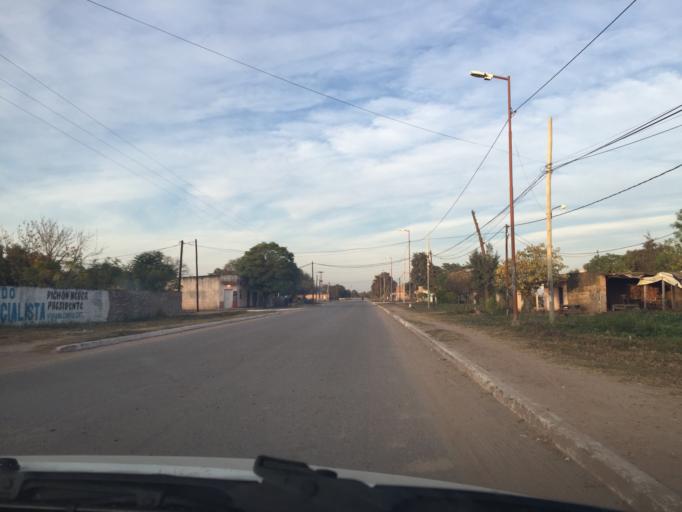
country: AR
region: Santiago del Estero
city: Pampa de los Guanacos
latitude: -26.2302
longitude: -61.8418
